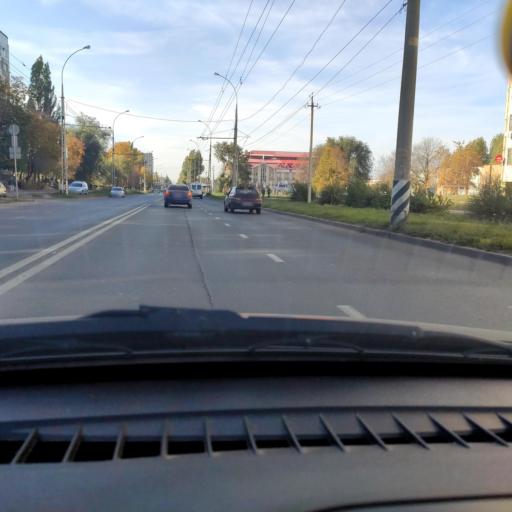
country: RU
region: Samara
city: Tol'yatti
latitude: 53.5356
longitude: 49.3071
